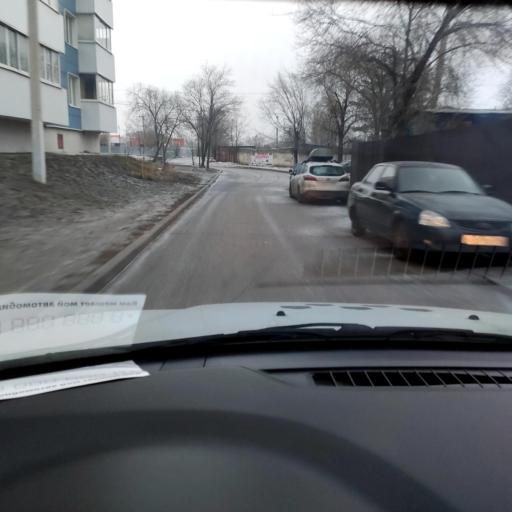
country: RU
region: Samara
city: Zhigulevsk
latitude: 53.4726
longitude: 49.4712
